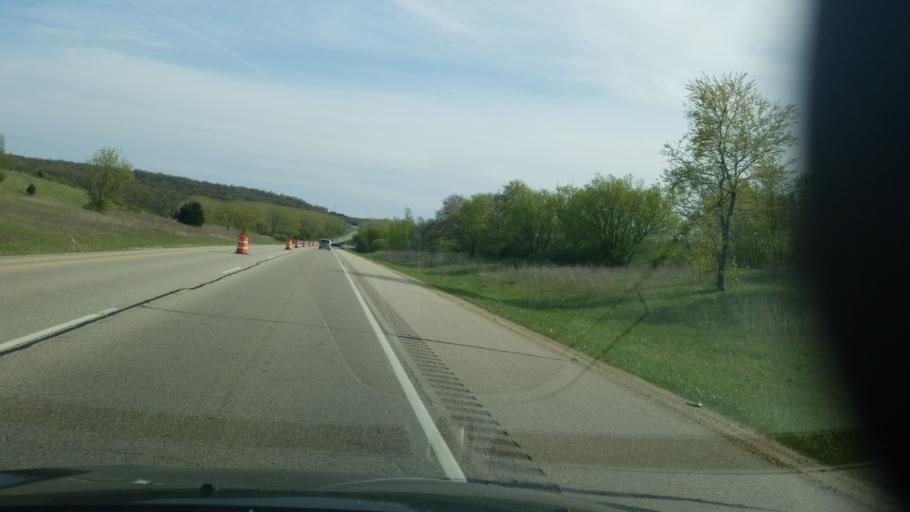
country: US
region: Wisconsin
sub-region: Dane County
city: Oregon
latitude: 42.9745
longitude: -89.3866
